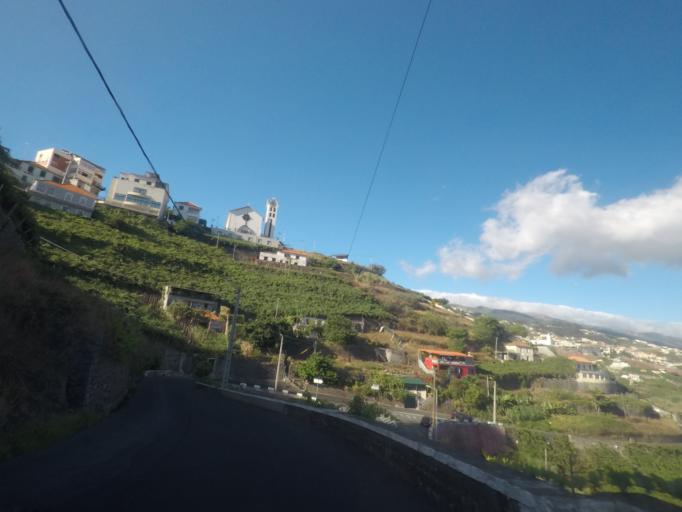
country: PT
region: Madeira
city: Camara de Lobos
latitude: 32.6668
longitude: -16.9886
